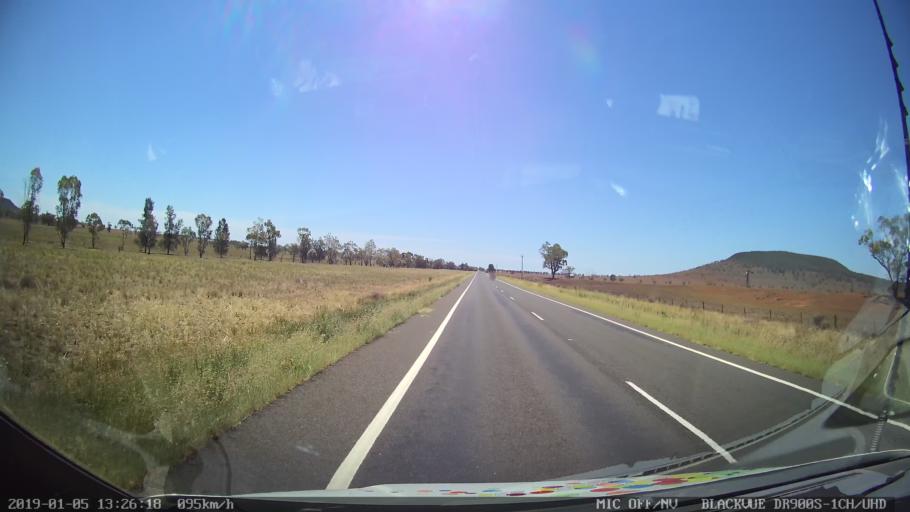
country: AU
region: New South Wales
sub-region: Gunnedah
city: Gunnedah
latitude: -31.0542
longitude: 150.0137
